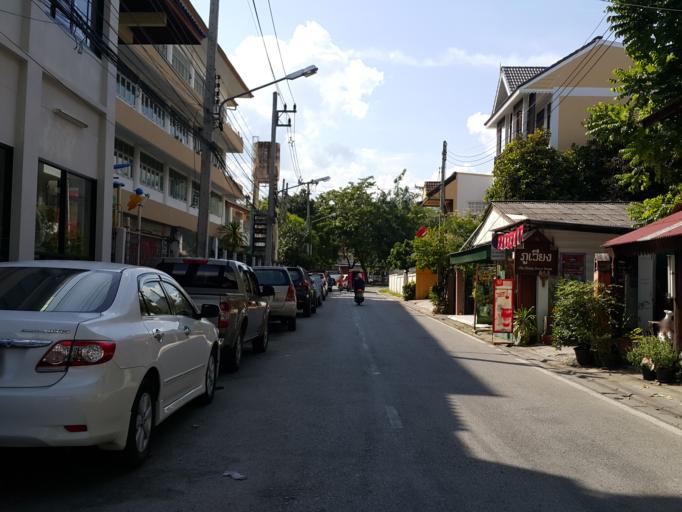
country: TH
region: Chiang Mai
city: Chiang Mai
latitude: 18.7877
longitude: 98.9791
